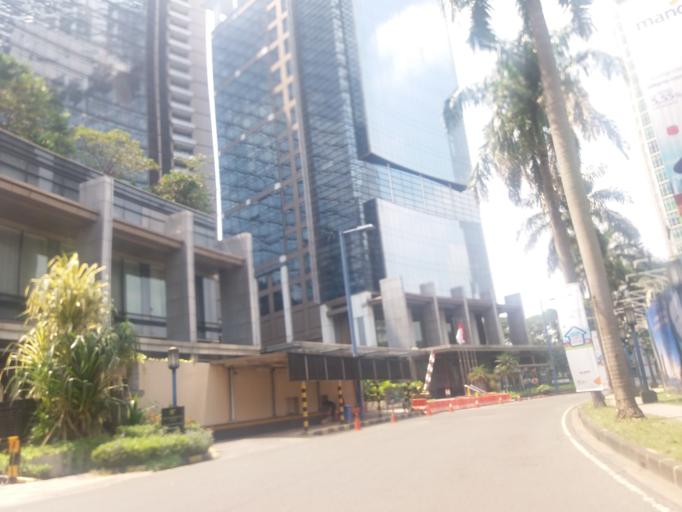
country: ID
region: Jakarta Raya
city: Jakarta
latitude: -6.2277
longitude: 106.8265
